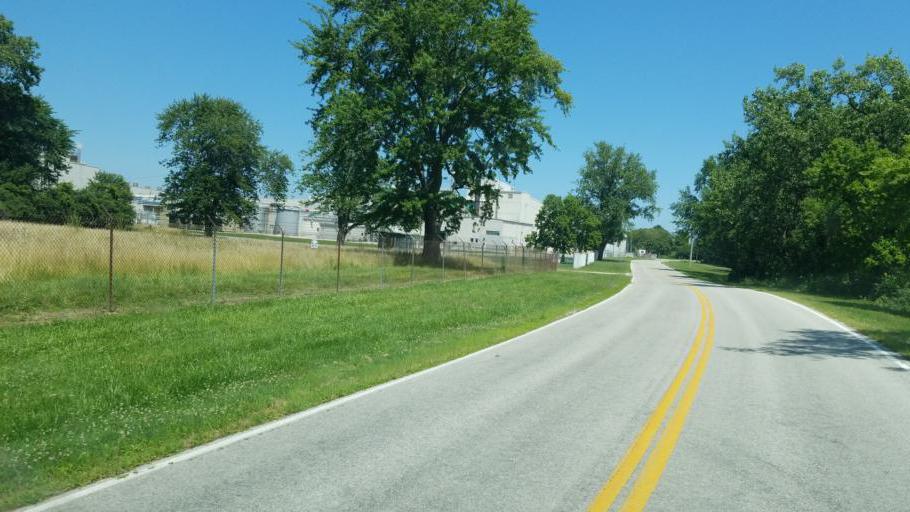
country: US
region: Ohio
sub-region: Ottawa County
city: Port Clinton
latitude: 41.4903
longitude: -82.8774
